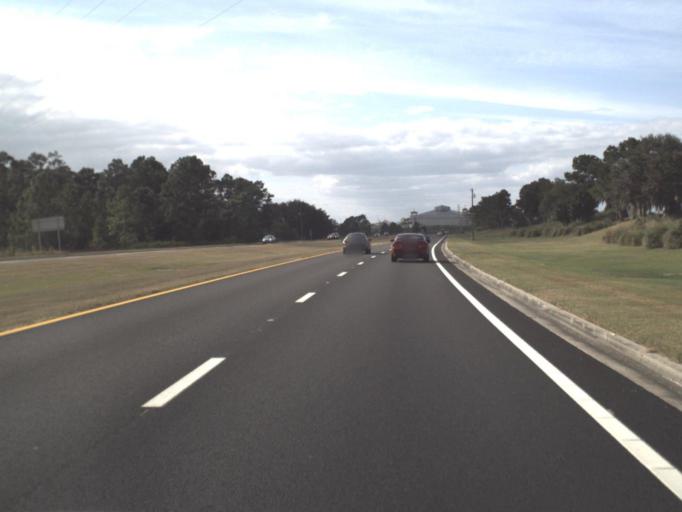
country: US
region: Florida
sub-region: Osceola County
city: Celebration
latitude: 28.3388
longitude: -81.5087
